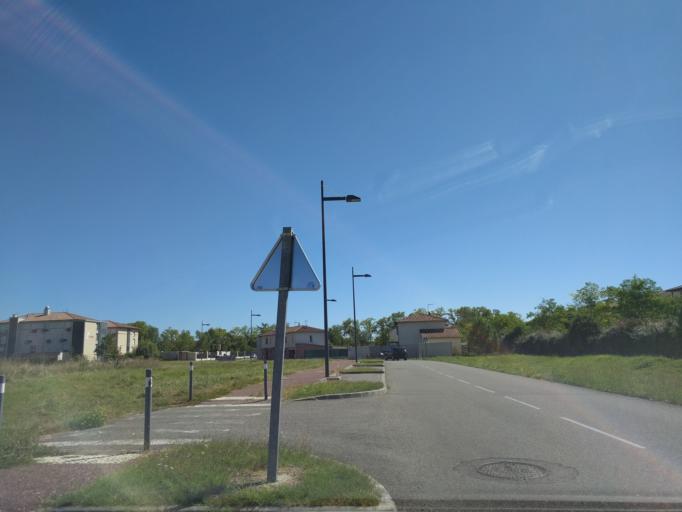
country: FR
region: Midi-Pyrenees
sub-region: Departement du Tarn-et-Garonne
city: Montauban
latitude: 44.0396
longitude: 1.3529
